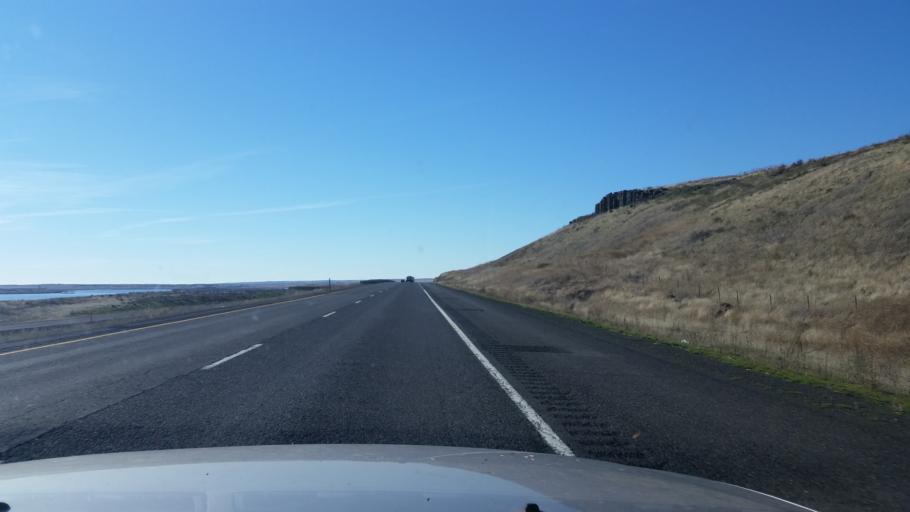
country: US
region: Washington
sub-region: Adams County
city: Ritzville
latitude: 47.2675
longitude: -118.0676
